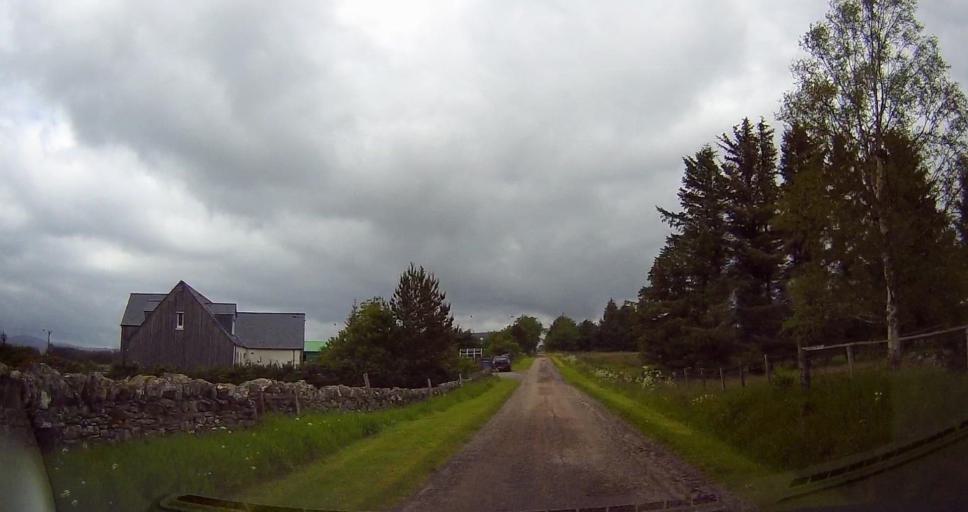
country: GB
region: Scotland
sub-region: Highland
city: Alness
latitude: 58.0742
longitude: -4.4389
